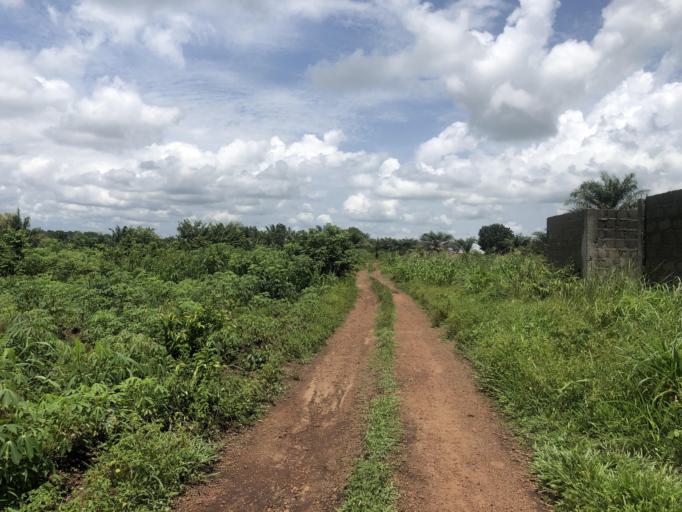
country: SL
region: Northern Province
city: Magburaka
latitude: 8.7109
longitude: -11.9403
